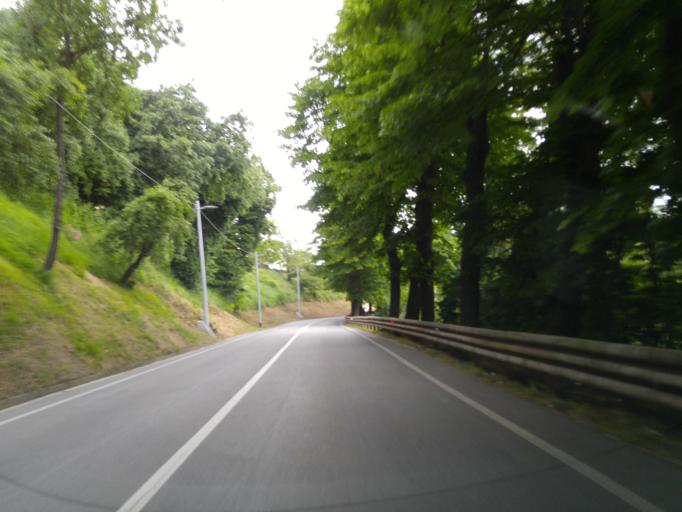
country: IT
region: The Marches
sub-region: Provincia di Pesaro e Urbino
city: Urbino
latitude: 43.7241
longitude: 12.6393
